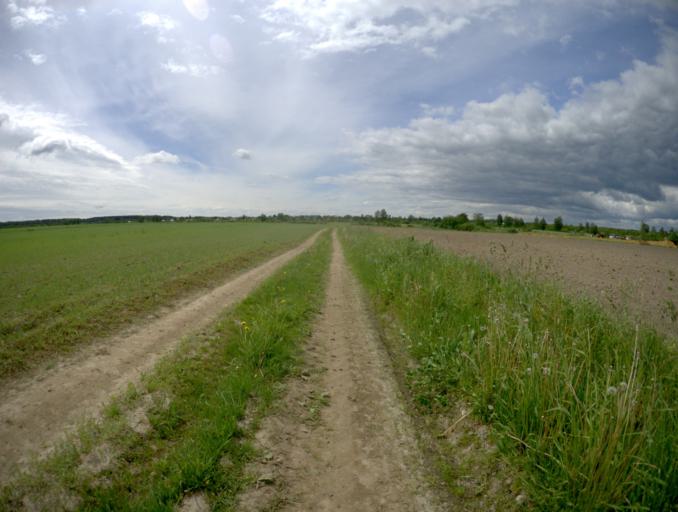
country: RU
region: Ivanovo
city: Savino
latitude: 56.5950
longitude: 41.2378
